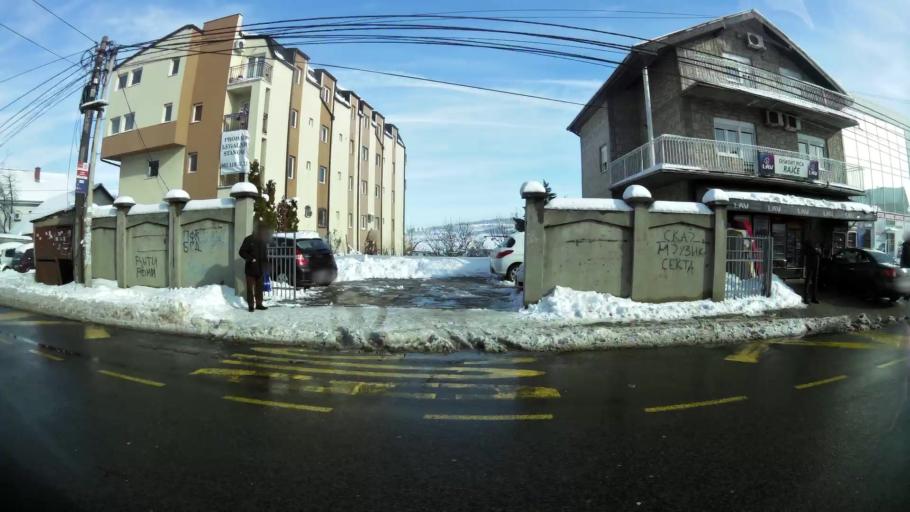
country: RS
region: Central Serbia
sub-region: Belgrade
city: Palilula
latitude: 44.8001
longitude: 20.5206
